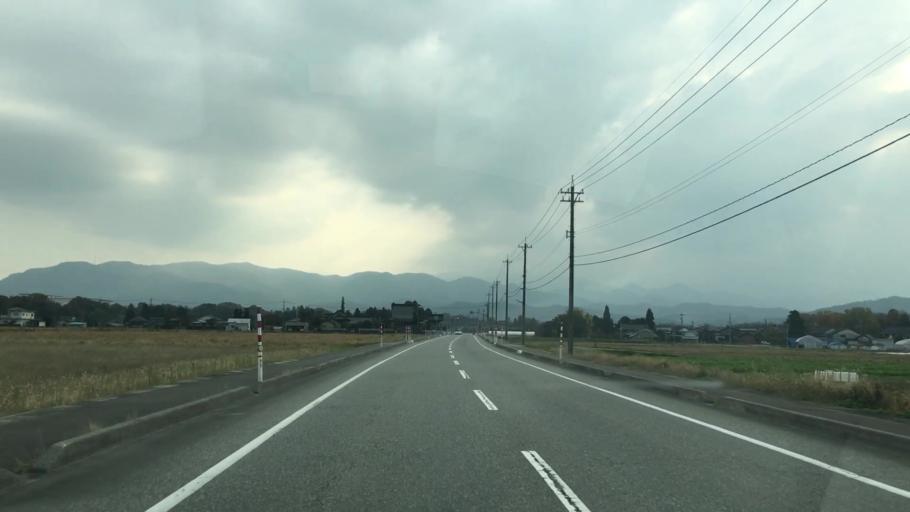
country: JP
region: Toyama
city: Yatsuomachi-higashikumisaka
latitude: 36.6060
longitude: 137.1922
